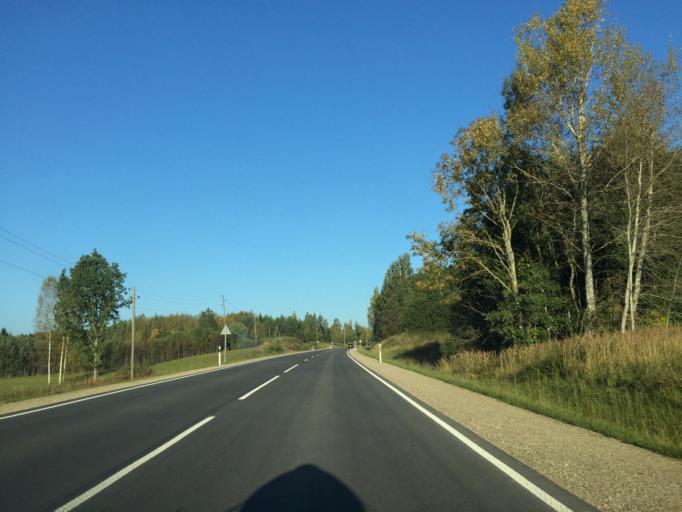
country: LV
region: Vecpiebalga
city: Vecpiebalga
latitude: 57.1105
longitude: 25.6979
